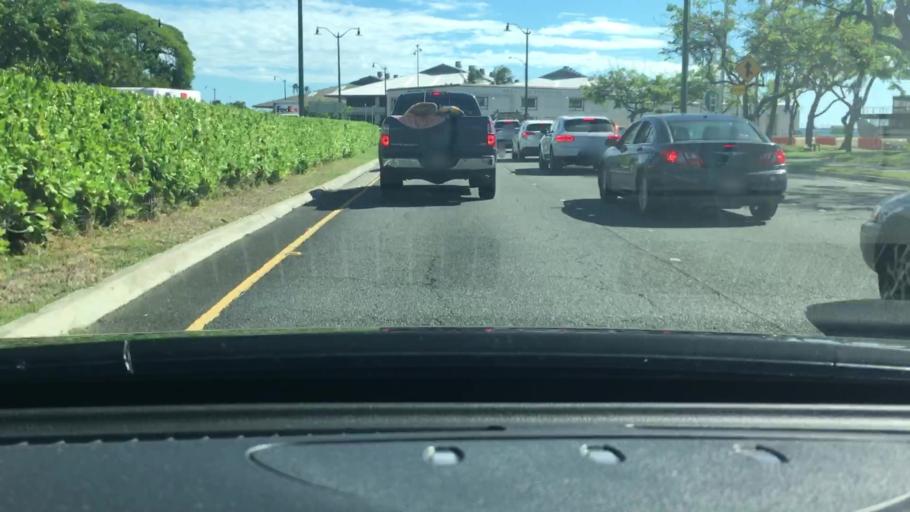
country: US
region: Hawaii
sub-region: Honolulu County
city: Honolulu
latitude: 21.3044
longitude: -157.8631
